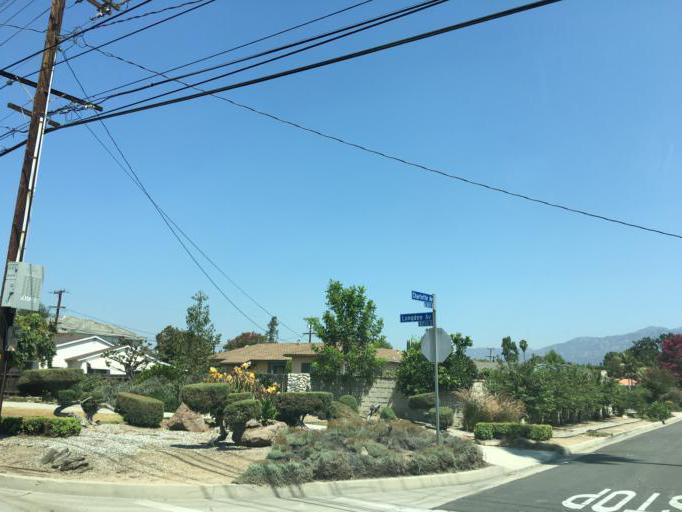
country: US
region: California
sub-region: Los Angeles County
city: San Marino
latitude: 34.1135
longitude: -118.0885
